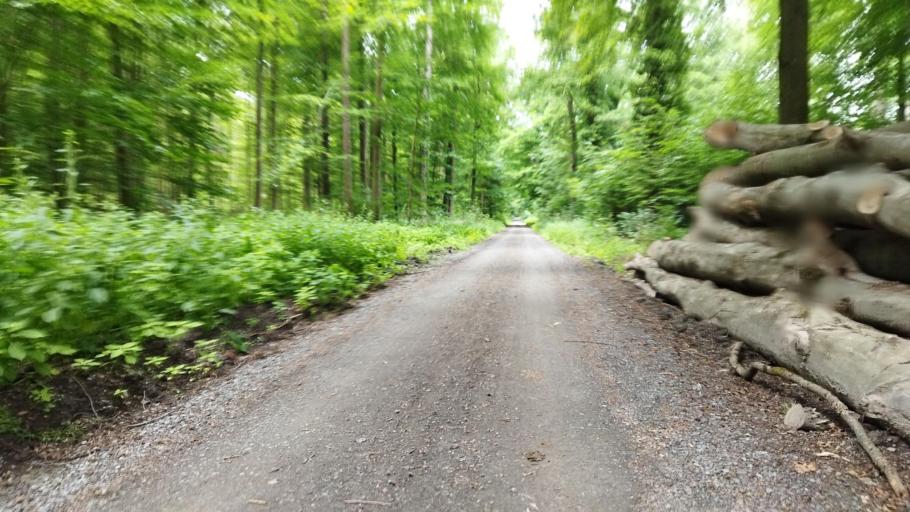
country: DE
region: Baden-Wuerttemberg
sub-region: Regierungsbezirk Stuttgart
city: Eppingen
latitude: 49.1040
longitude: 8.9350
